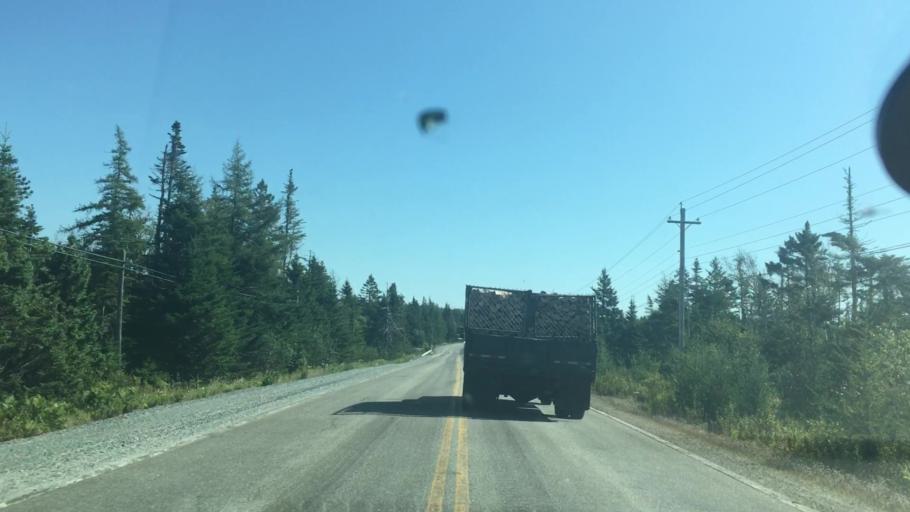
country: CA
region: Nova Scotia
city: New Glasgow
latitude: 44.9035
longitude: -62.4554
